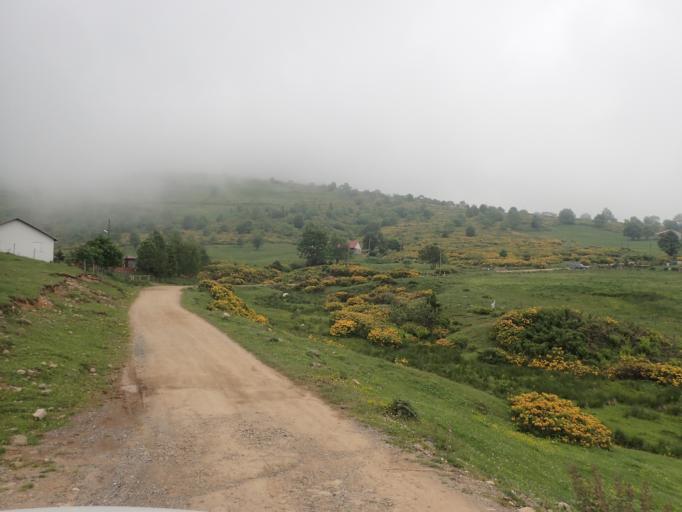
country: TR
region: Ordu
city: Topcam
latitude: 40.6684
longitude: 37.9333
